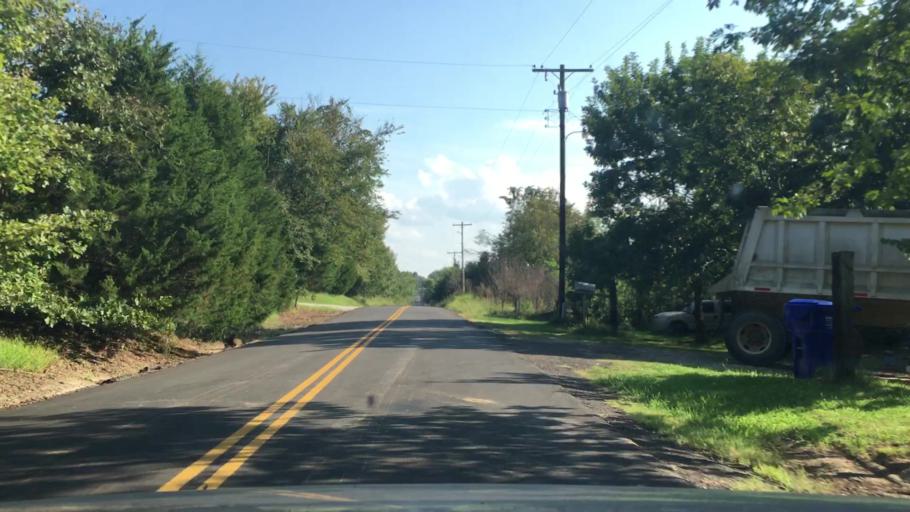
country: US
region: Oklahoma
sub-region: Muskogee County
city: Fort Gibson
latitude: 35.6505
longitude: -95.2161
